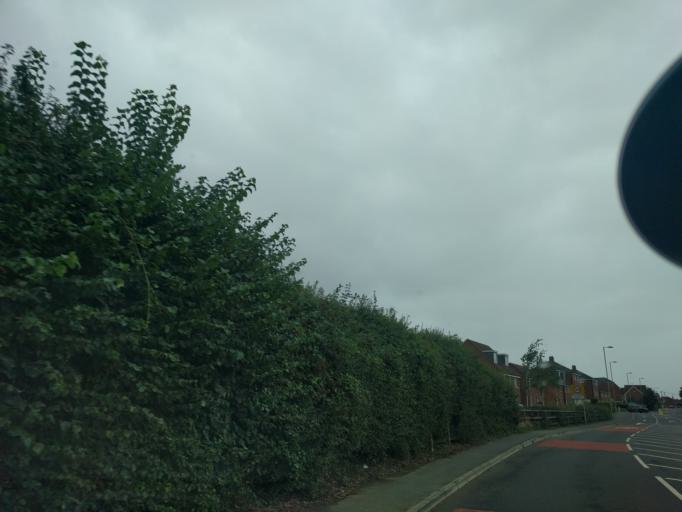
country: GB
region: England
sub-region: Wiltshire
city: Melksham
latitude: 51.3770
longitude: -2.1189
